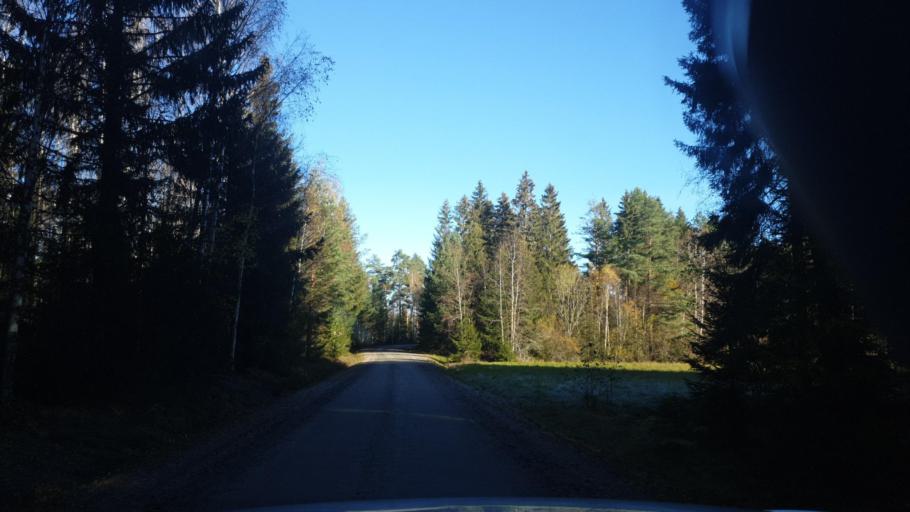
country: SE
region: Vaermland
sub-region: Karlstads Kommun
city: Edsvalla
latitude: 59.4882
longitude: 13.1638
